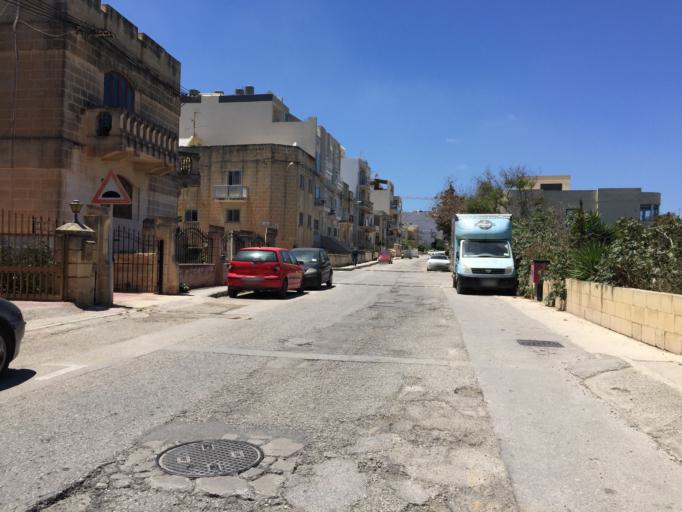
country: MT
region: Is-Swieqi
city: Swieqi
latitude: 35.9232
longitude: 14.4827
